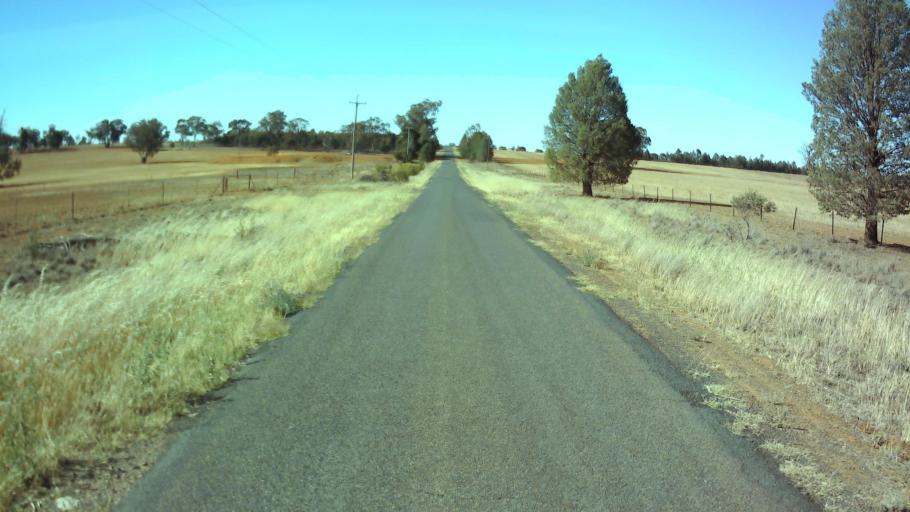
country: AU
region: New South Wales
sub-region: Weddin
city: Grenfell
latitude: -33.7604
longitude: 147.8296
